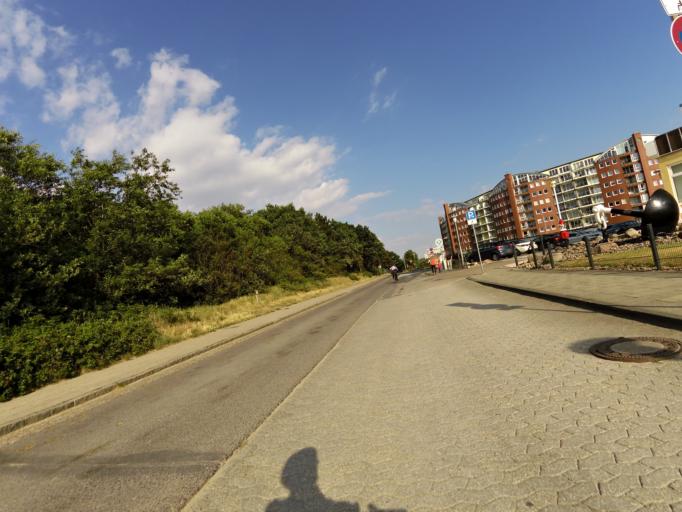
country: DE
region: Lower Saxony
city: Nordholz
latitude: 53.8629
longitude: 8.5970
